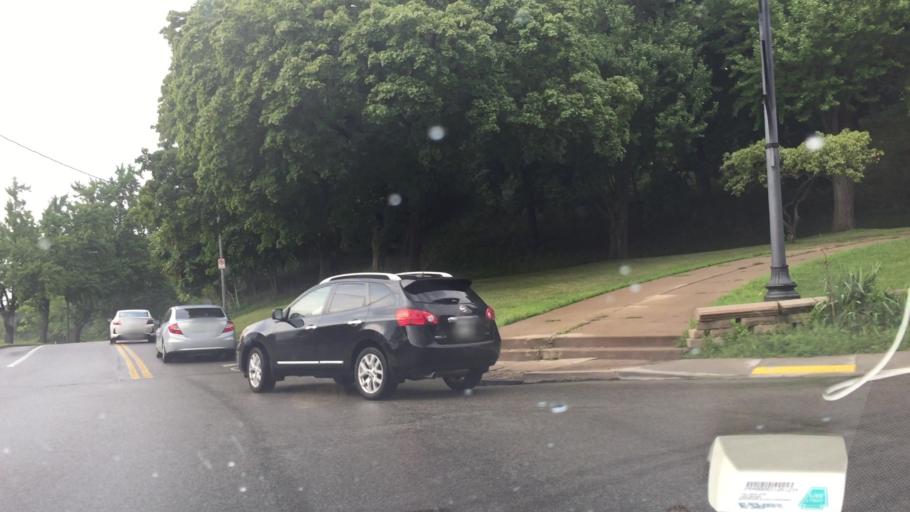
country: US
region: Pennsylvania
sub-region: Allegheny County
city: Sharpsburg
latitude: 40.4798
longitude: -79.9196
